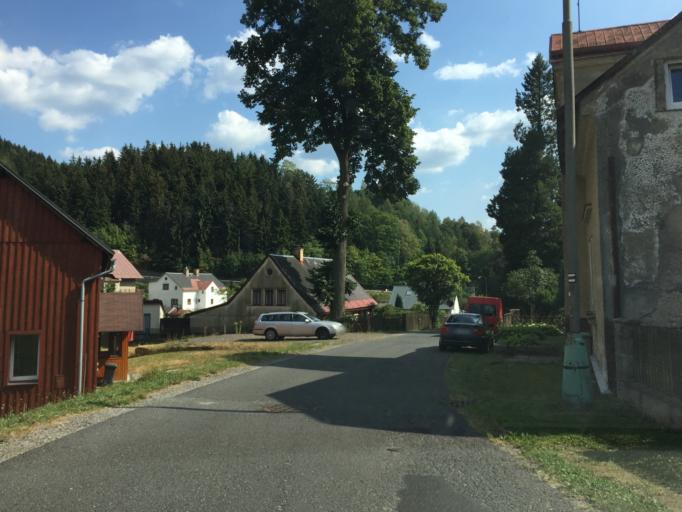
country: CZ
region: Liberecky
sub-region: Okres Jablonec nad Nisou
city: Janov nad Nisou
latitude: 50.7722
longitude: 15.1672
